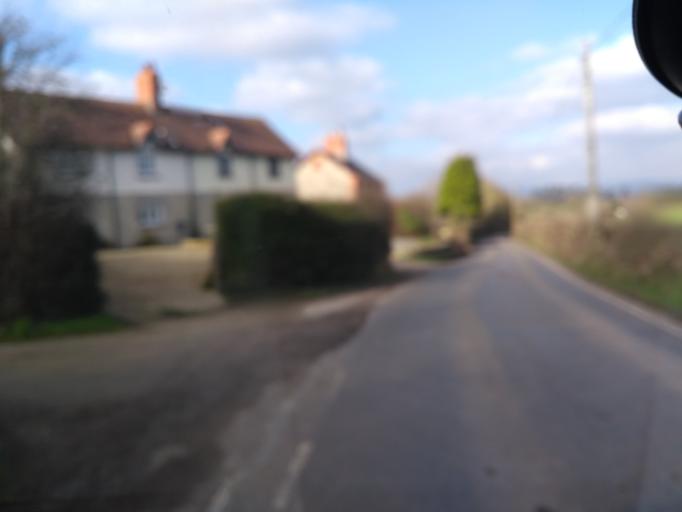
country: GB
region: England
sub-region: Somerset
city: Creech Saint Michael
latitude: 50.9726
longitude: -3.0535
